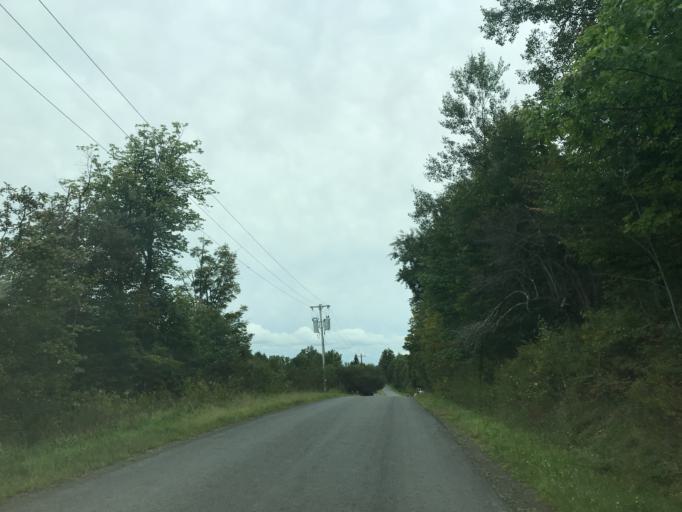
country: US
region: New York
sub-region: Otsego County
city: Worcester
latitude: 42.5757
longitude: -74.6718
